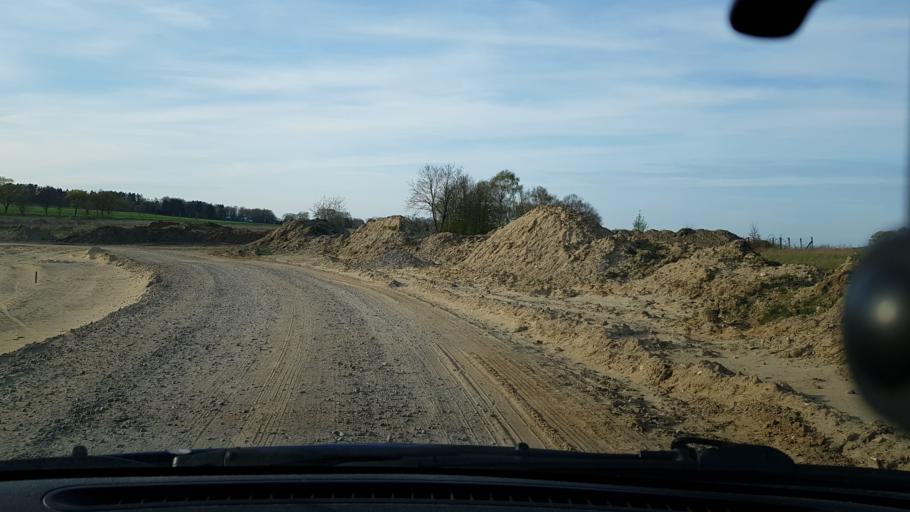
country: DE
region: Lower Saxony
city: Buchholz in der Nordheide
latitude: 53.3582
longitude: 9.8727
